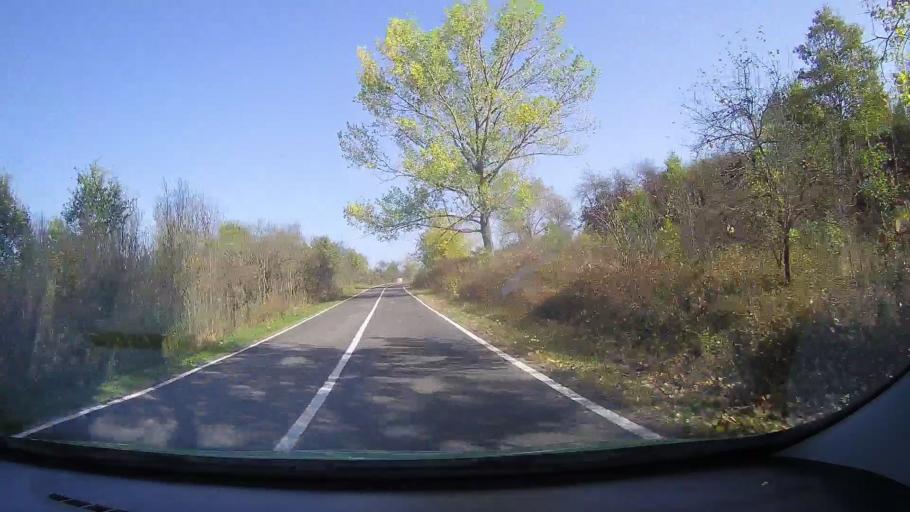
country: RO
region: Timis
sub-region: Comuna Curtea
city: Curtea
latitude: 45.8444
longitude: 22.3125
